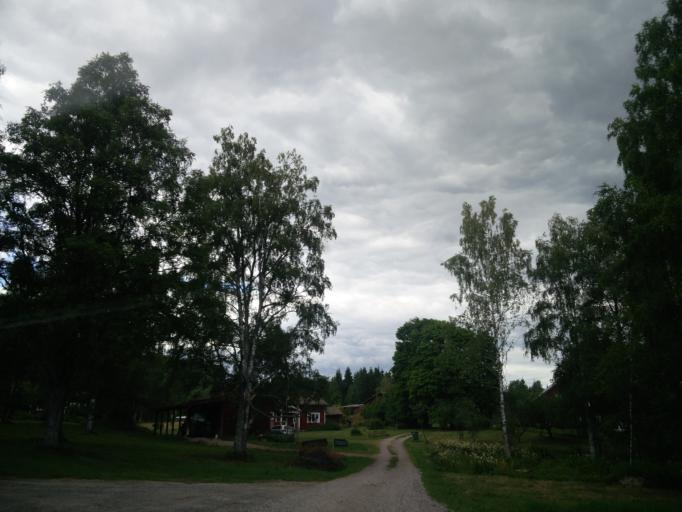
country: SE
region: OErebro
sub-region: Ljusnarsbergs Kommun
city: Kopparberg
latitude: 59.8390
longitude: 14.8073
